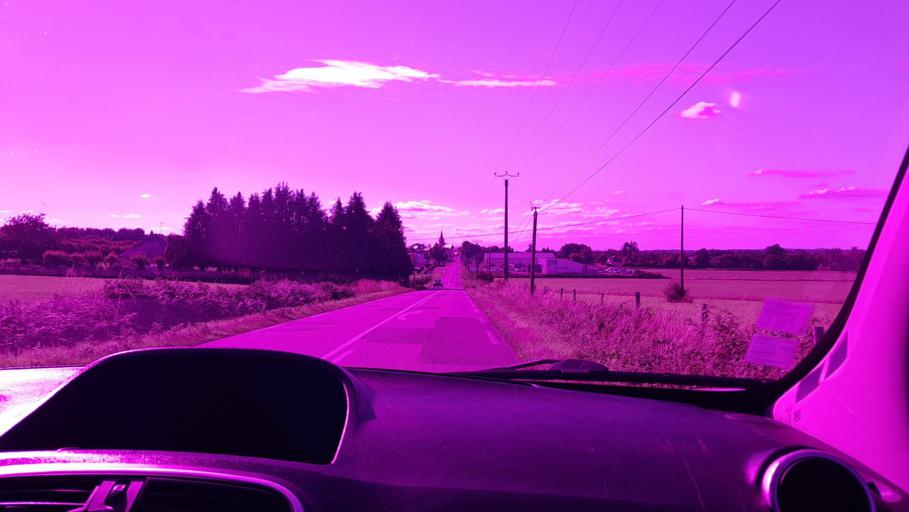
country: FR
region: Pays de la Loire
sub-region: Departement de la Mayenne
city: Ballots
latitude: 47.8903
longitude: -1.0381
